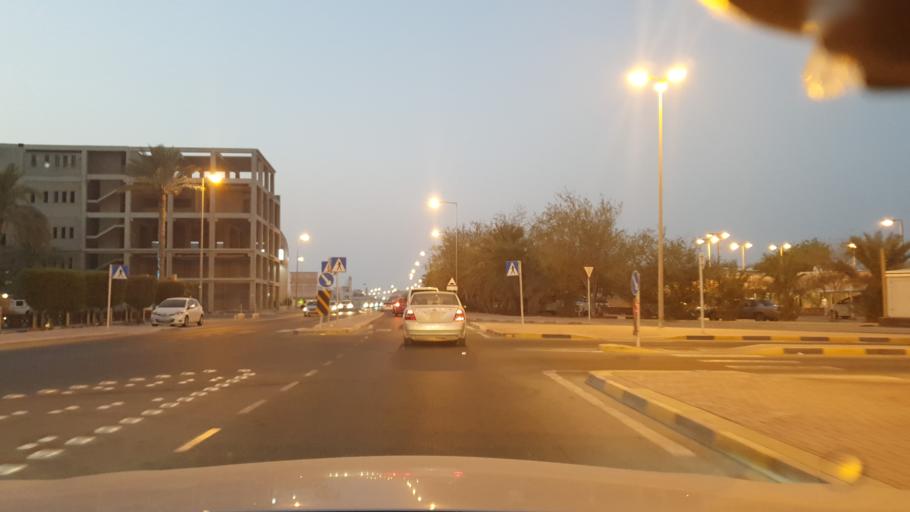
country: BH
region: Muharraq
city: Al Muharraq
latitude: 26.2674
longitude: 50.6157
